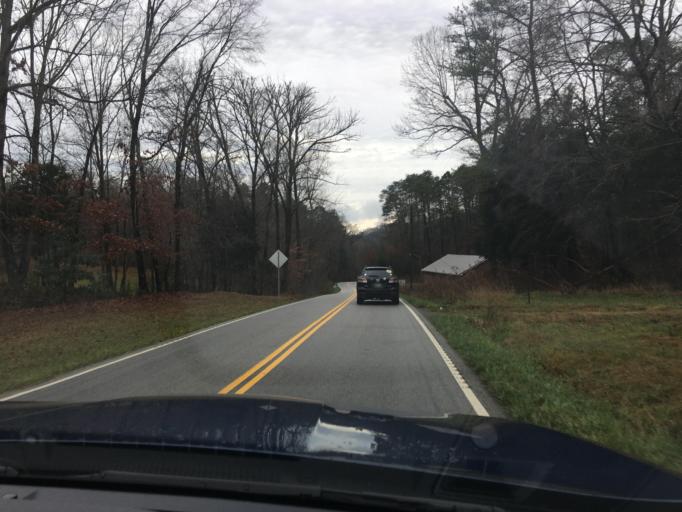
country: US
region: Tennessee
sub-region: McMinn County
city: Englewood
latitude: 35.3490
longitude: -84.4010
